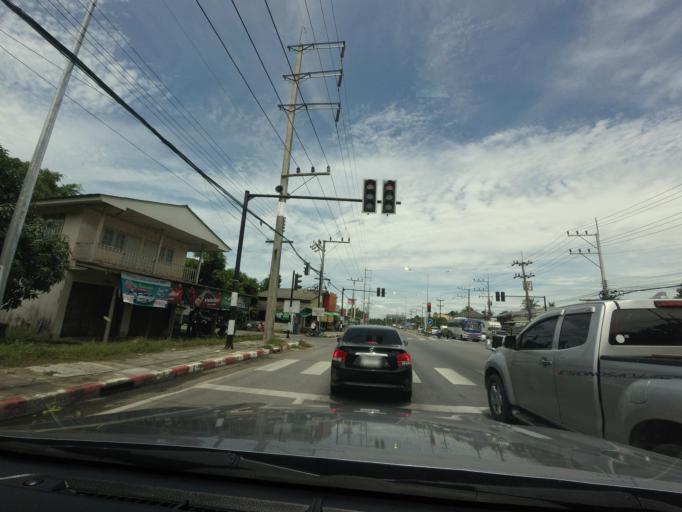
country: TH
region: Songkhla
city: Krasae Sin
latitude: 7.6019
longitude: 100.4009
